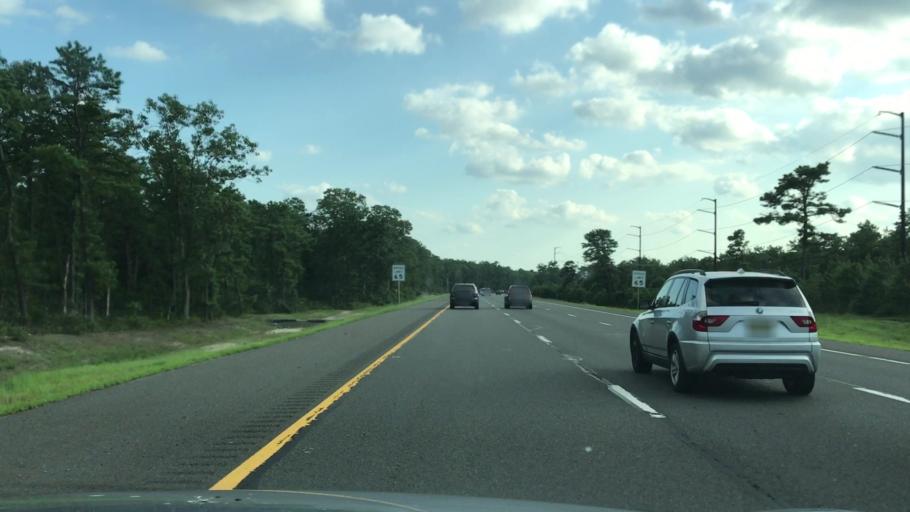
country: US
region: New Jersey
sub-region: Ocean County
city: Manahawkin
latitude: 39.7053
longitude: -74.2865
